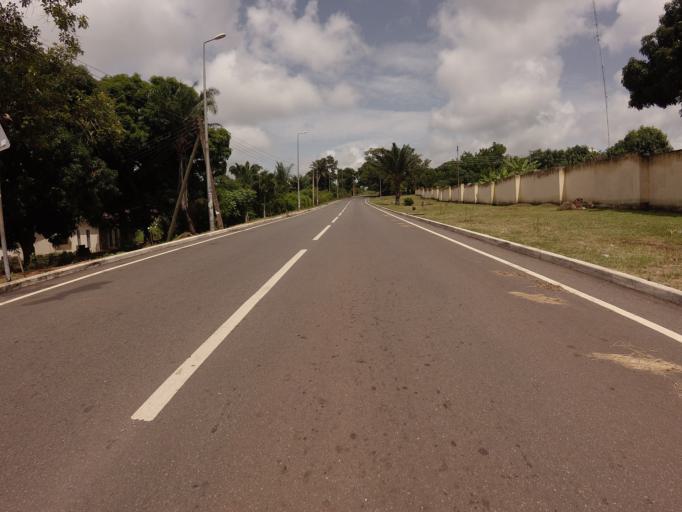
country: GH
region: Volta
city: Ho
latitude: 6.6080
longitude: 0.4645
